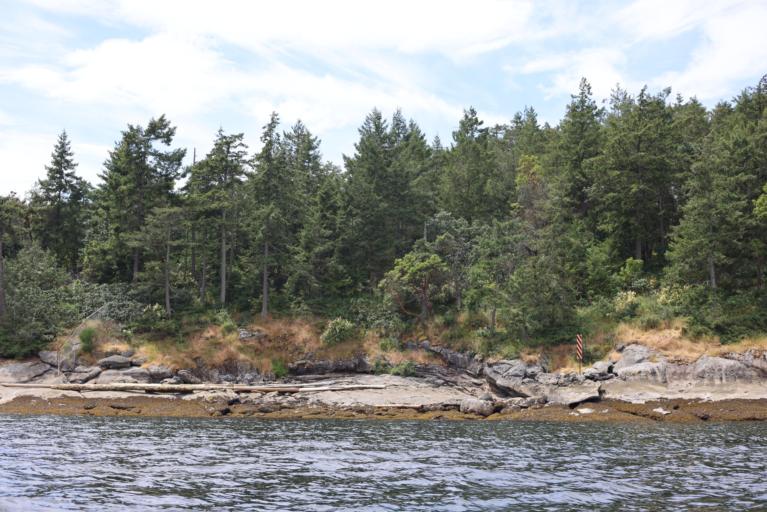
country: CA
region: British Columbia
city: Nanaimo
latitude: 49.1655
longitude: -123.8920
